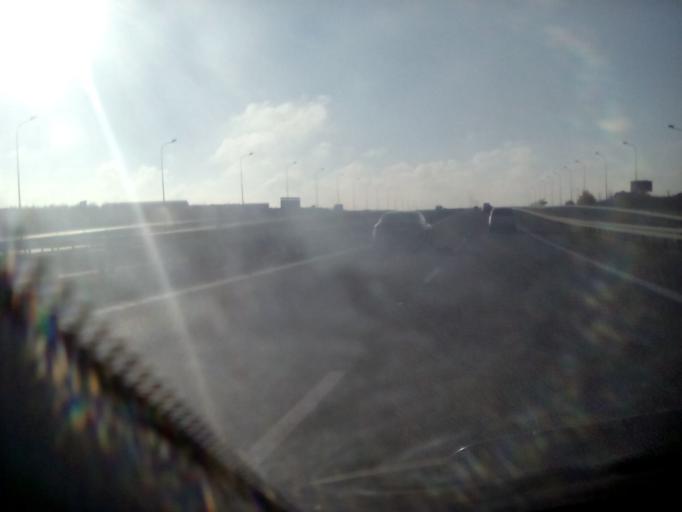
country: PL
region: Masovian Voivodeship
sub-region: Powiat grojecki
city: Grojec
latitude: 51.8336
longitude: 20.8775
